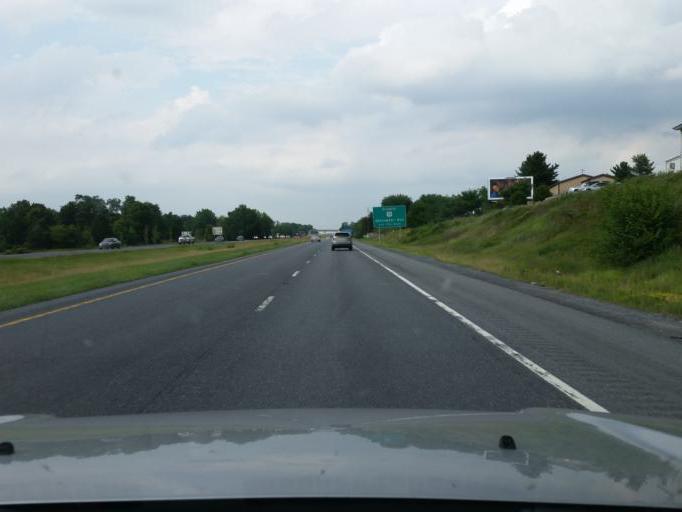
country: US
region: Maryland
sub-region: Frederick County
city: Emmitsburg
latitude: 39.7161
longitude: -77.3087
